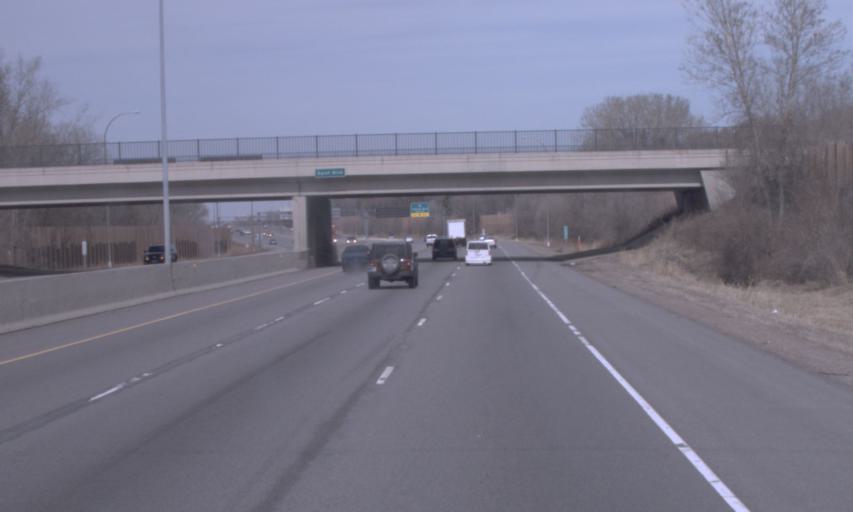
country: US
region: Minnesota
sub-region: Anoka County
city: Coon Rapids
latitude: 45.1623
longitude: -93.2842
